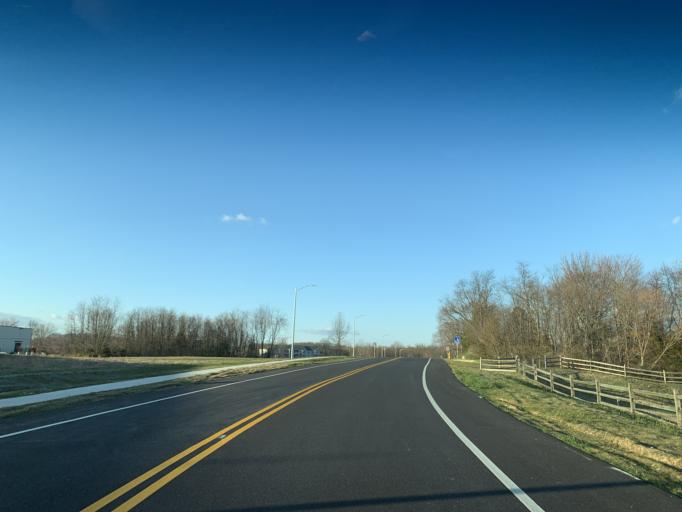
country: US
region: Maryland
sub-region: Harford County
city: Aberdeen
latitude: 39.5237
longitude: -76.1790
